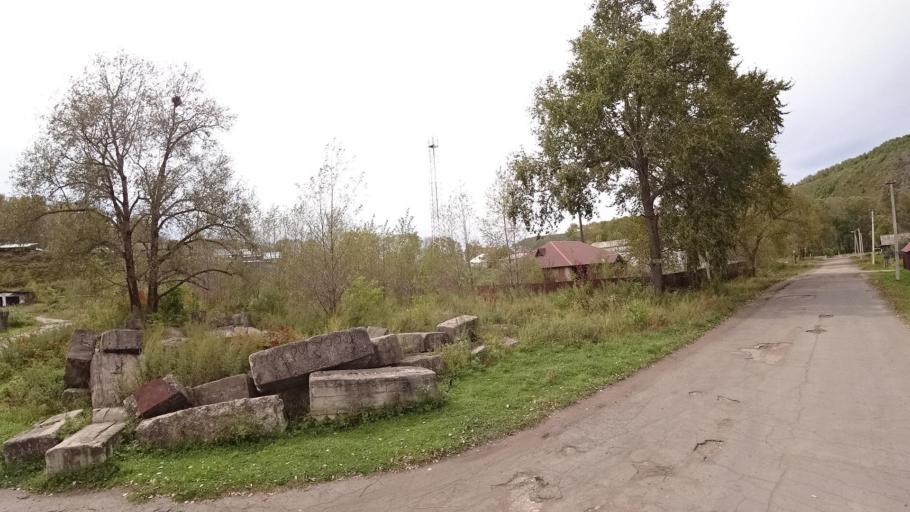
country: RU
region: Jewish Autonomous Oblast
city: Khingansk
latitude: 49.1265
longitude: 131.1971
